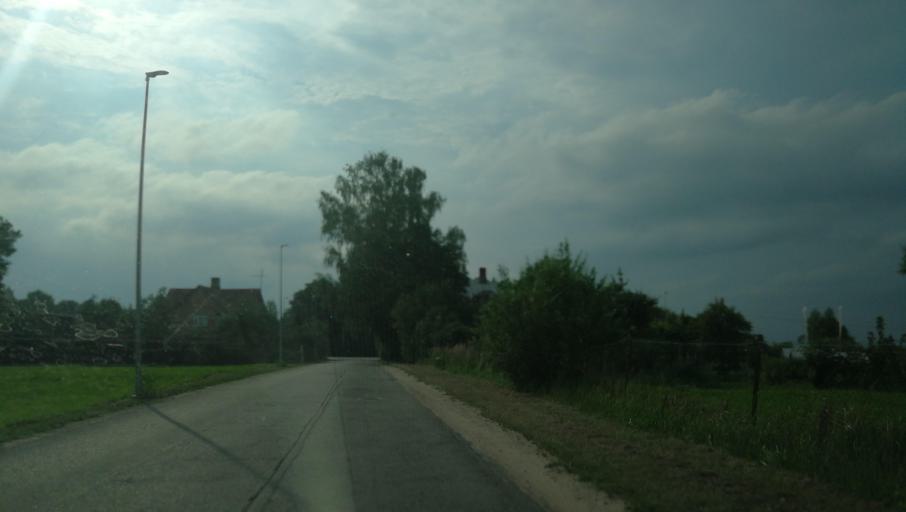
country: LV
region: Cesu Rajons
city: Cesis
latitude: 57.3204
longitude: 25.2966
